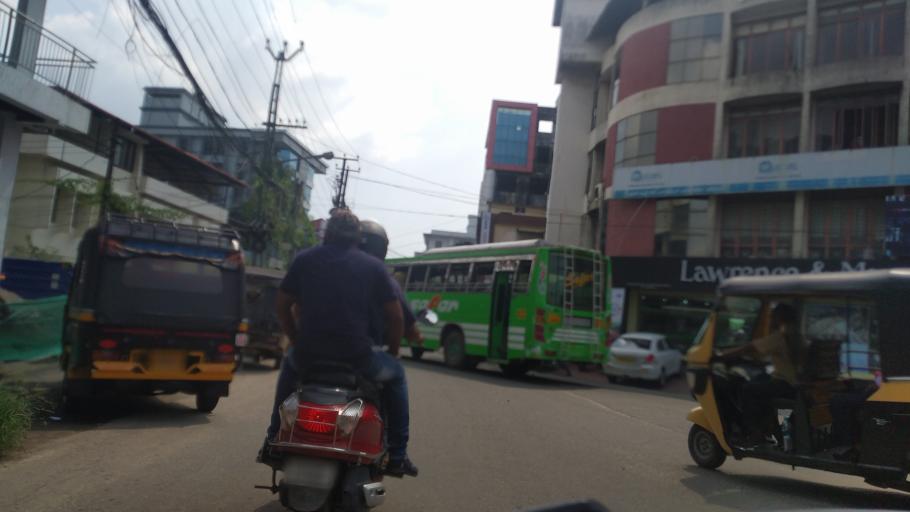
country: IN
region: Kerala
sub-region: Ernakulam
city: Cochin
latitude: 9.9723
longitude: 76.2861
